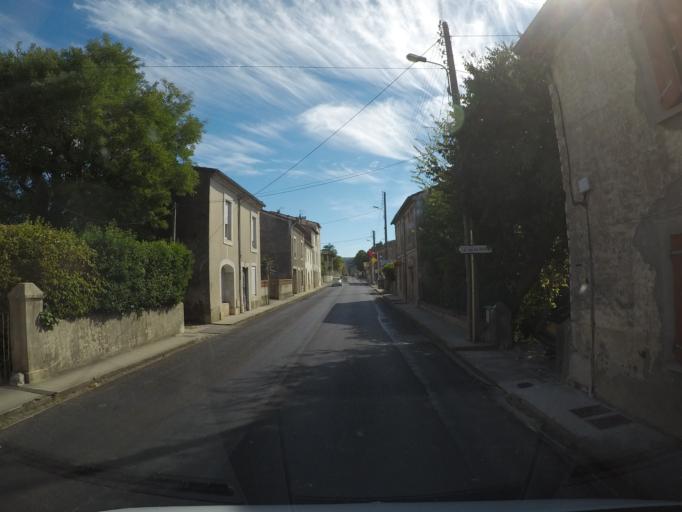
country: FR
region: Languedoc-Roussillon
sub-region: Departement de l'Herault
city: Saint-Bauzille-de-Putois
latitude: 43.8972
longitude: 3.7371
